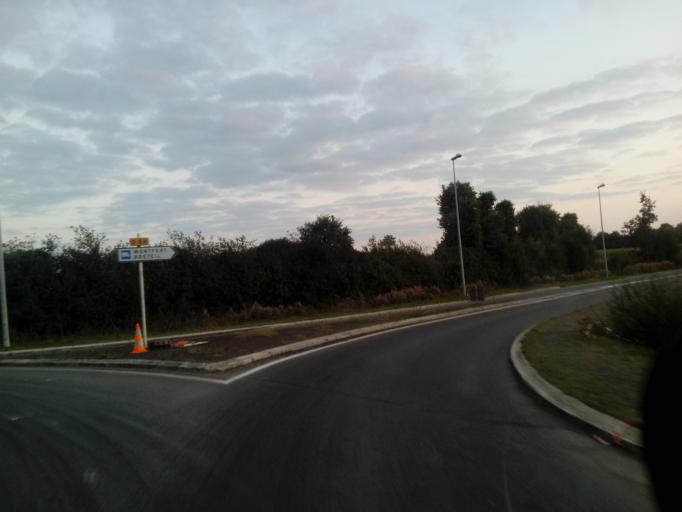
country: FR
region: Brittany
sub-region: Departement d'Ille-et-Vilaine
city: Pleumeleuc
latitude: 48.1761
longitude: -1.9259
